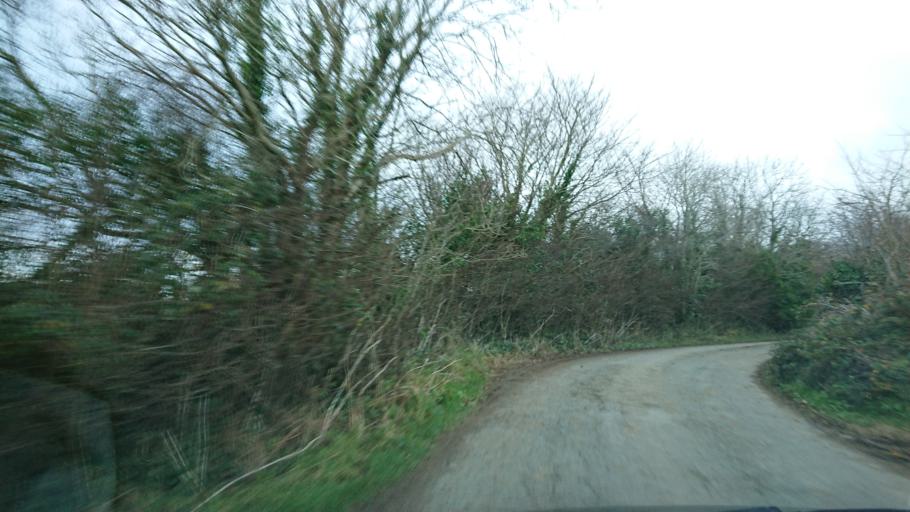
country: IE
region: Munster
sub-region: Waterford
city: Dunmore East
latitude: 52.1884
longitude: -7.0430
